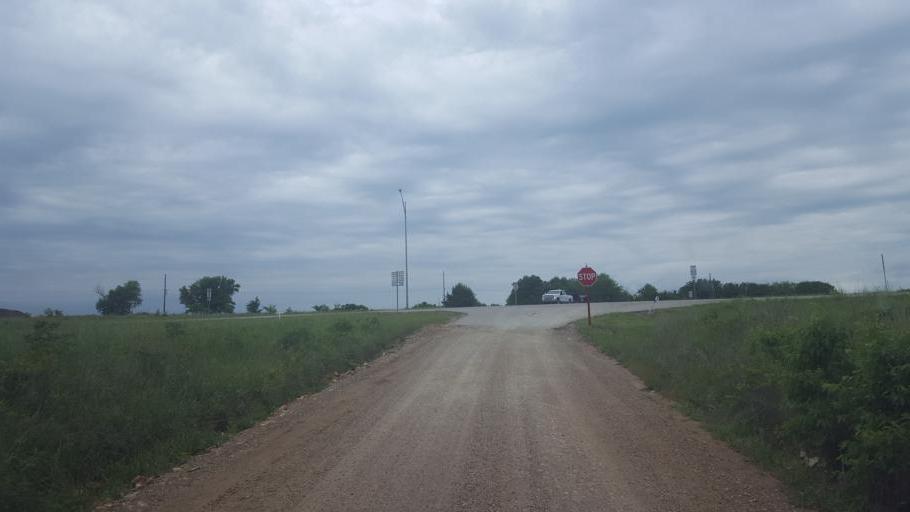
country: US
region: Missouri
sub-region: Moniteau County
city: California
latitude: 38.6345
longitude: -92.6187
